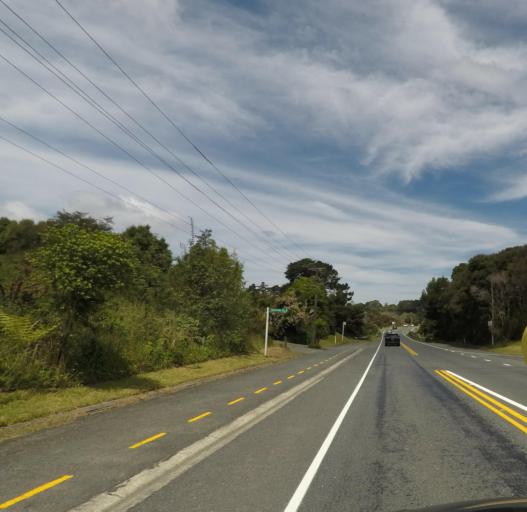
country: NZ
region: Auckland
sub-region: Auckland
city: Rothesay Bay
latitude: -36.6822
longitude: 174.6987
